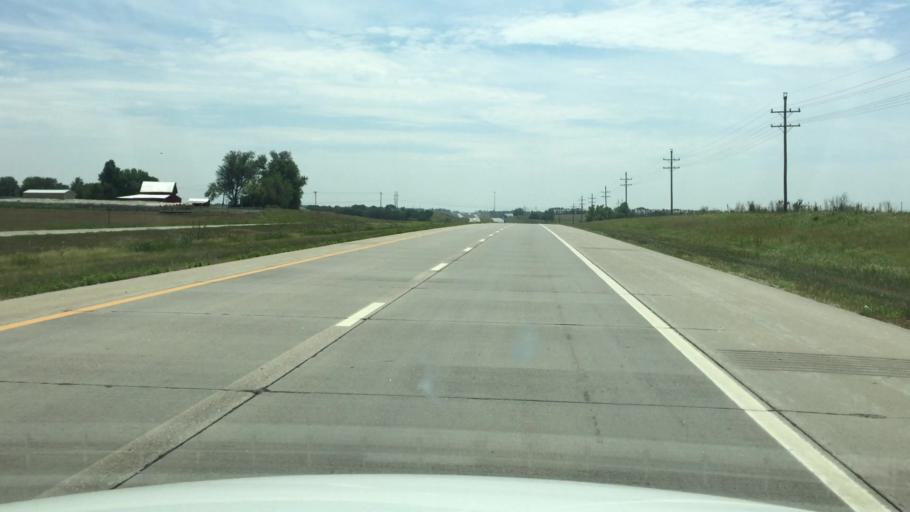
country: US
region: Kansas
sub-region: Jackson County
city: Holton
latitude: 39.2785
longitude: -95.7197
